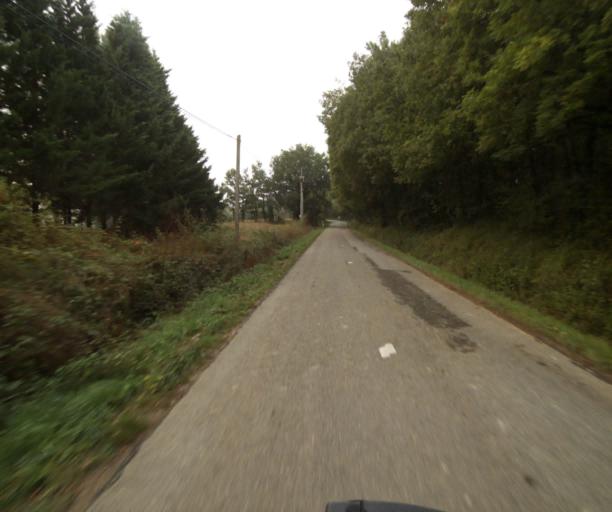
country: FR
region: Midi-Pyrenees
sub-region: Departement du Tarn-et-Garonne
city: Saint-Nauphary
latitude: 43.9417
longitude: 1.4416
